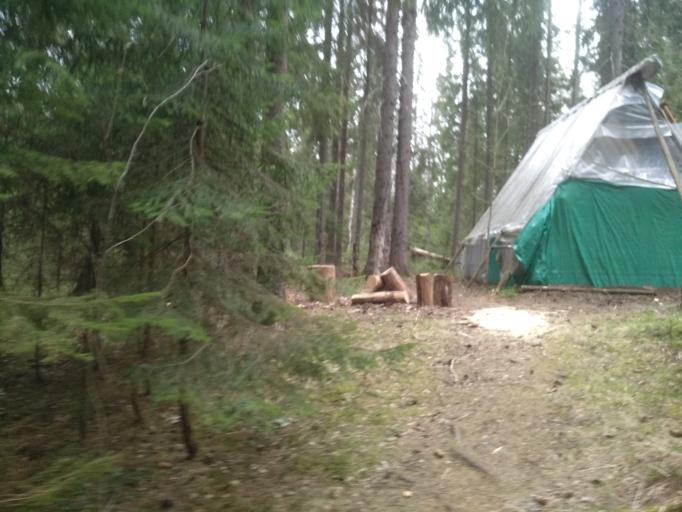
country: RU
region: Leningrad
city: Sosnovo
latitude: 60.4833
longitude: 30.1554
